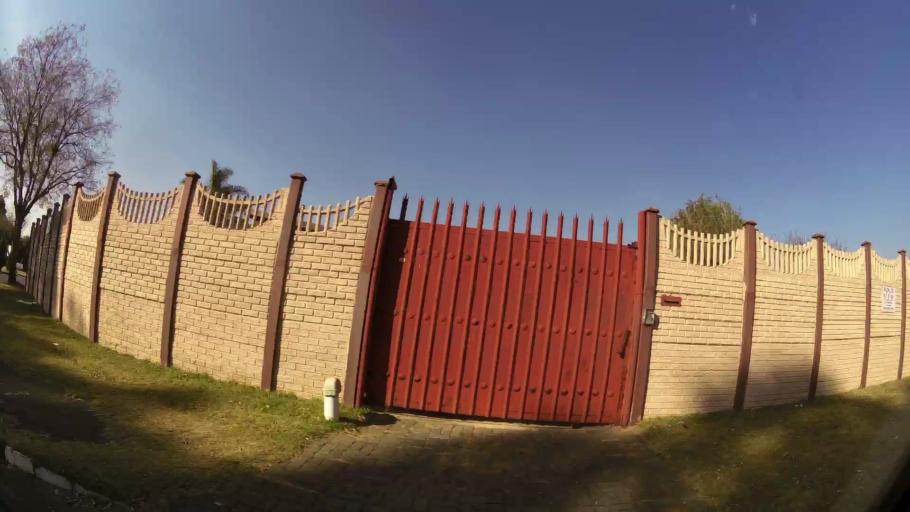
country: ZA
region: Gauteng
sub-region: City of Johannesburg Metropolitan Municipality
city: Johannesburg
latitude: -26.2521
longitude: 28.0090
